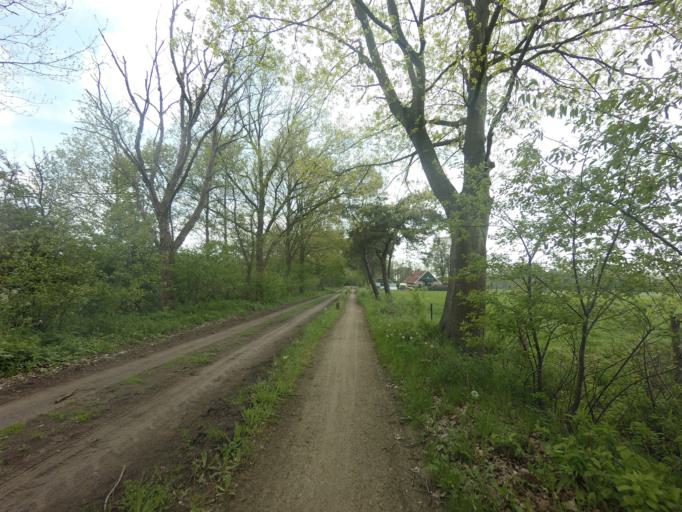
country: NL
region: Overijssel
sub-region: Gemeente Haaksbergen
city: Haaksbergen
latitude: 52.1288
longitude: 6.7379
